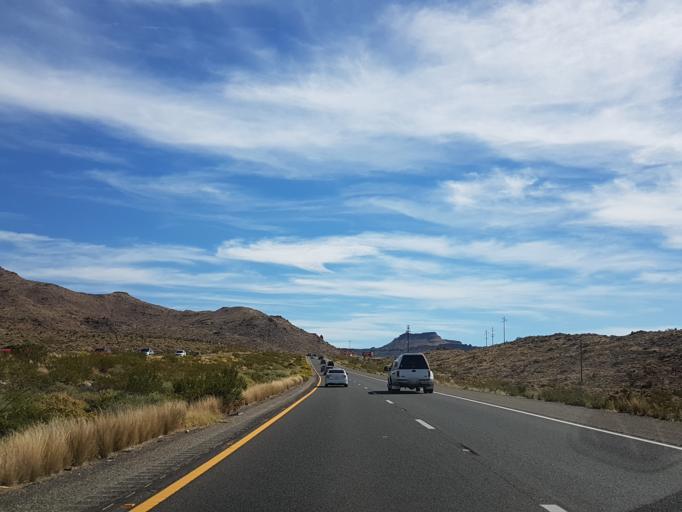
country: US
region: Arizona
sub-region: Mohave County
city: Golden Valley
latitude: 35.2401
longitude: -114.1456
